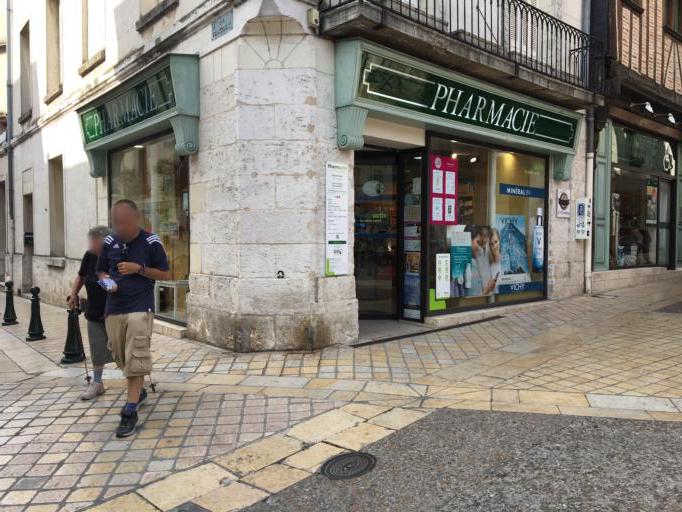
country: FR
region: Centre
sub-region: Departement d'Indre-et-Loire
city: Amboise
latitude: 47.4129
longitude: 0.9843
